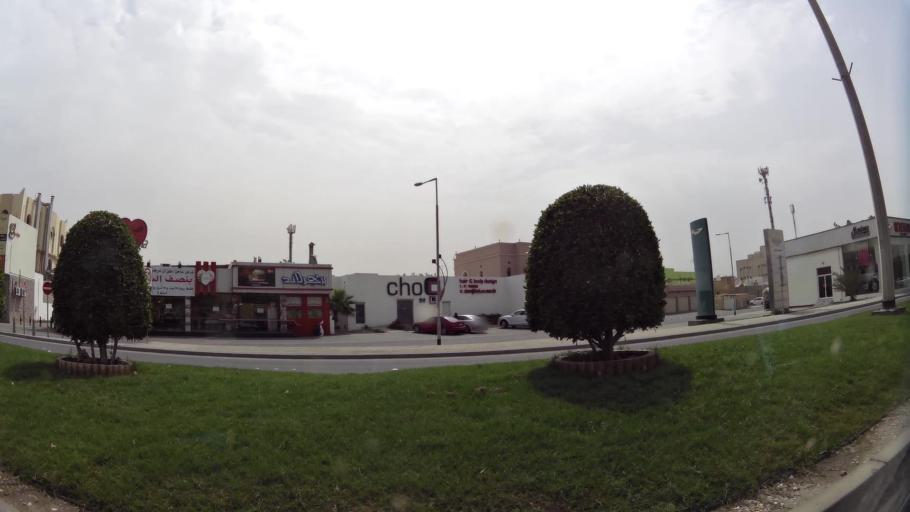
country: BH
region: Northern
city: Ar Rifa'
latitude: 26.1318
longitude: 50.5444
